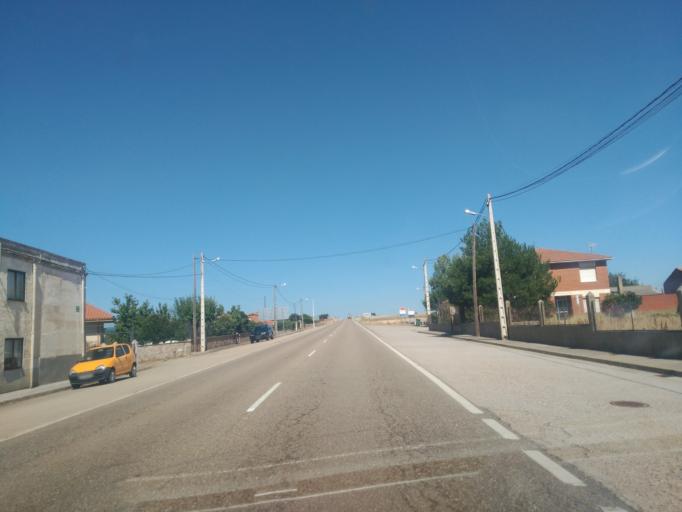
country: ES
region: Castille and Leon
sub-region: Provincia de Zamora
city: Pozuelo de Tabara
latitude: 41.7868
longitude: -5.8979
